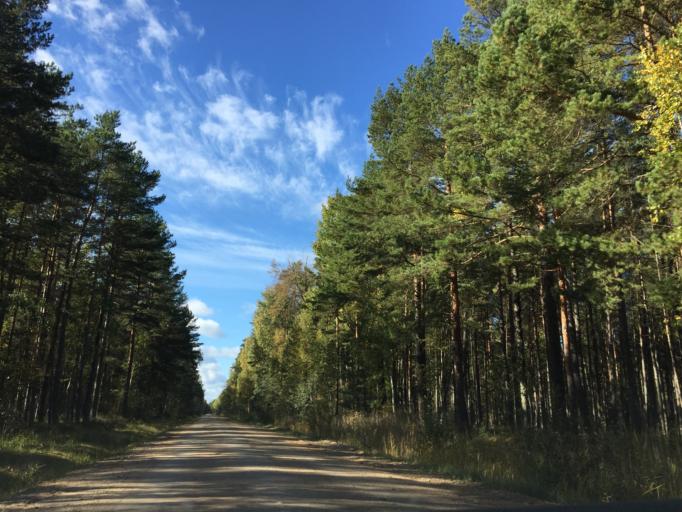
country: LV
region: Mesraga
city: Mersrags
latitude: 57.2599
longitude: 23.1546
